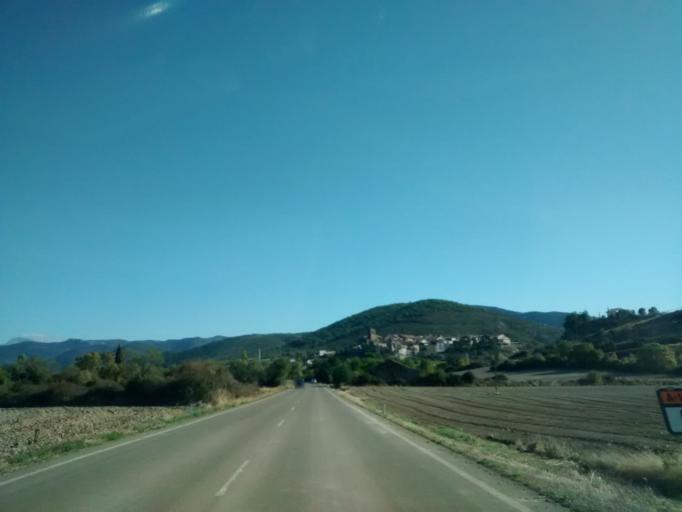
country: ES
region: Aragon
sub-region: Provincia de Huesca
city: Santa Cruz de la Seros
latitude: 42.5835
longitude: -0.7409
